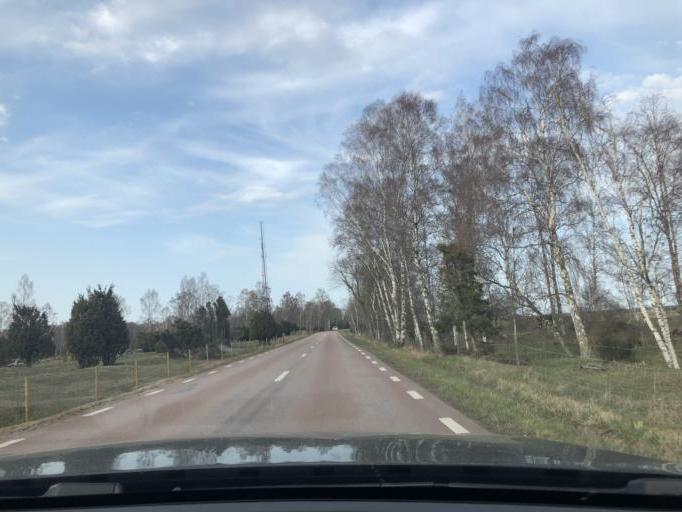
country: SE
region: Kalmar
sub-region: Morbylanga Kommun
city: Sodra Sandby
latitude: 56.5494
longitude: 16.6128
